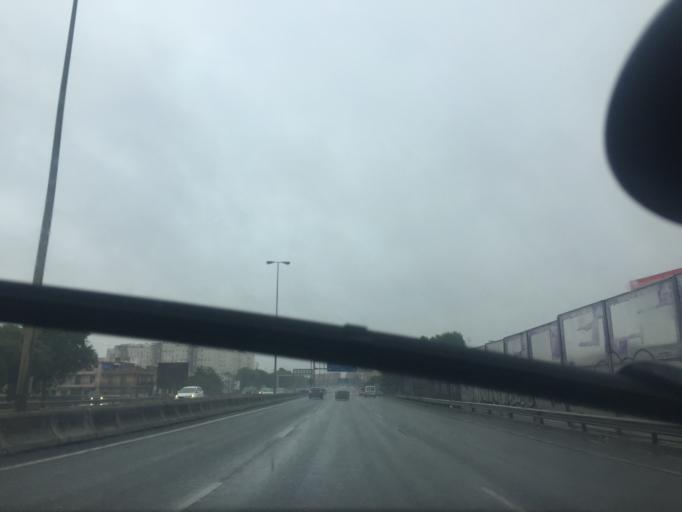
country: ES
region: Andalusia
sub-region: Provincia de Sevilla
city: Sevilla
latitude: 37.3841
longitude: -5.9415
